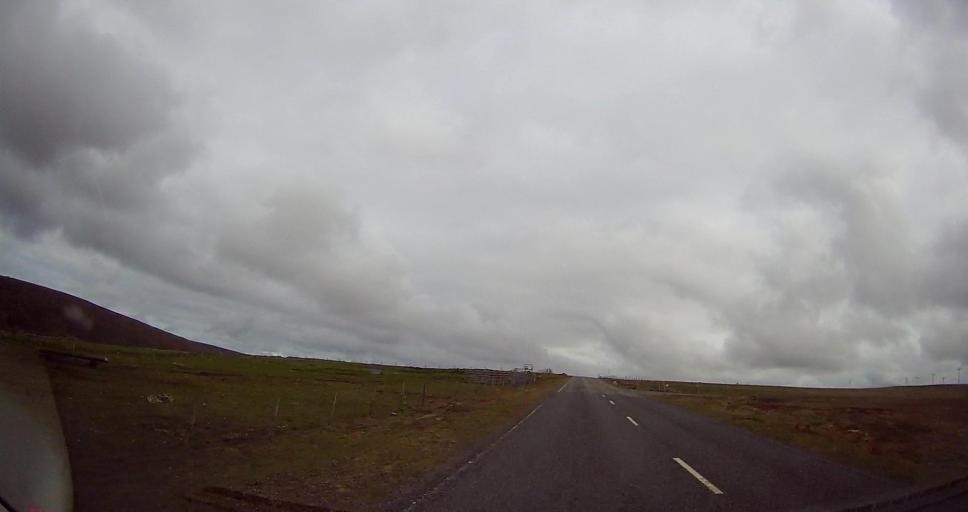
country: GB
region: Scotland
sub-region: Shetland Islands
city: Shetland
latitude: 60.7330
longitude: -0.8951
